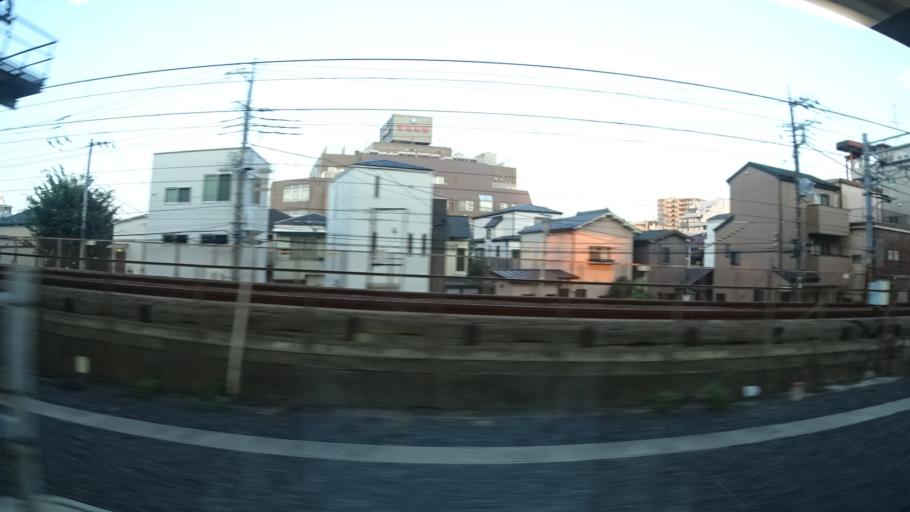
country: JP
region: Saitama
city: Soka
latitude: 35.7460
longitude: 139.8036
